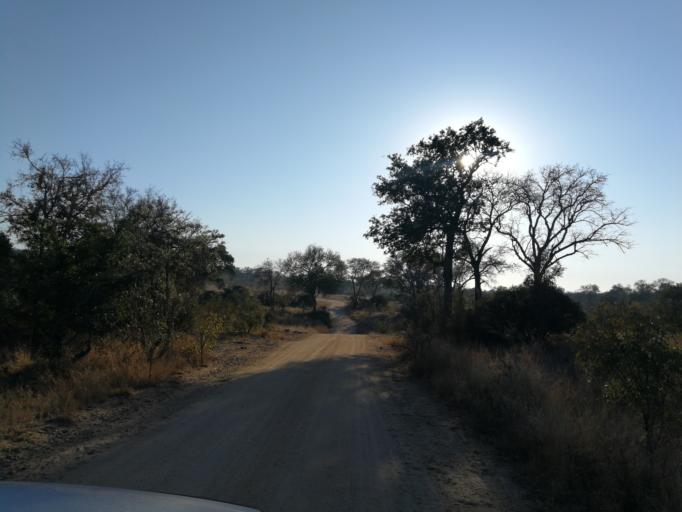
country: ZA
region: Limpopo
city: Thulamahashi
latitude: -25.0115
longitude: 31.4303
